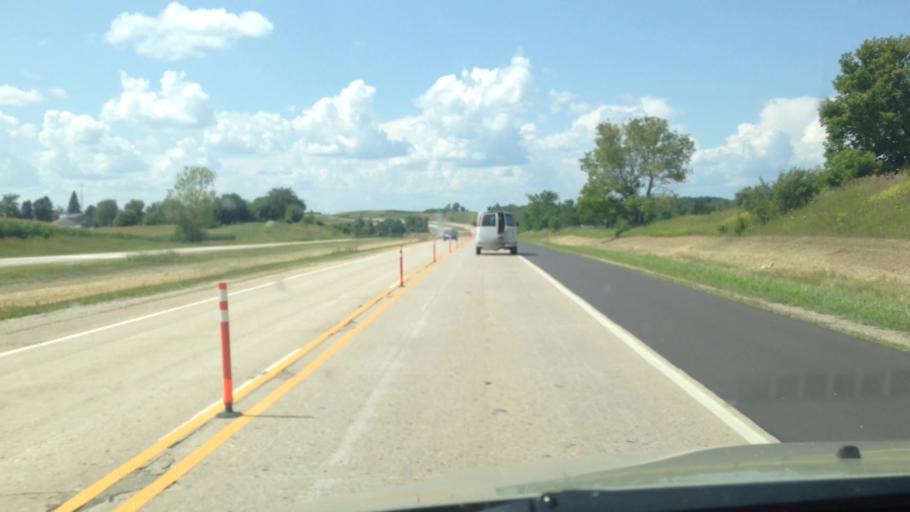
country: US
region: Wisconsin
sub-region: Shawano County
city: Bonduel
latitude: 44.7140
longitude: -88.3884
